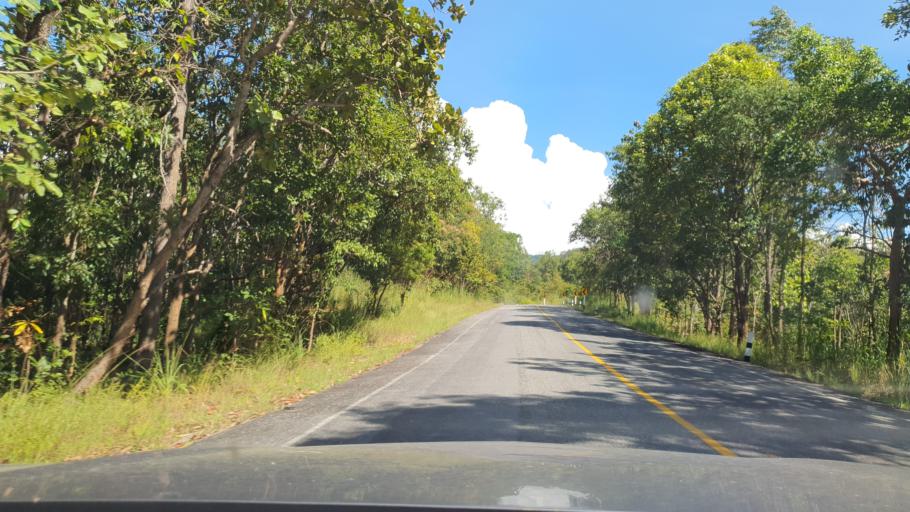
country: TH
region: Chiang Mai
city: Phrao
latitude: 19.3591
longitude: 99.2598
